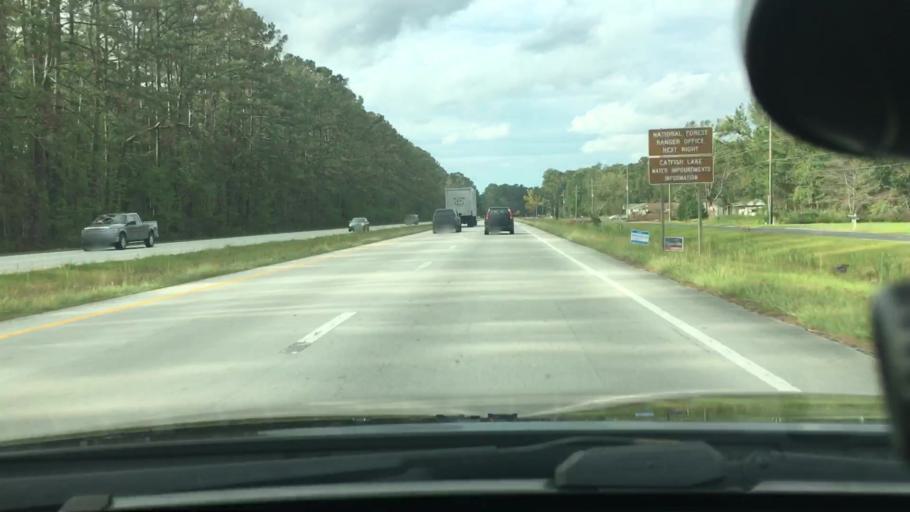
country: US
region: North Carolina
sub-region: Craven County
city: Neuse Forest
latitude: 34.9846
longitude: -76.9796
